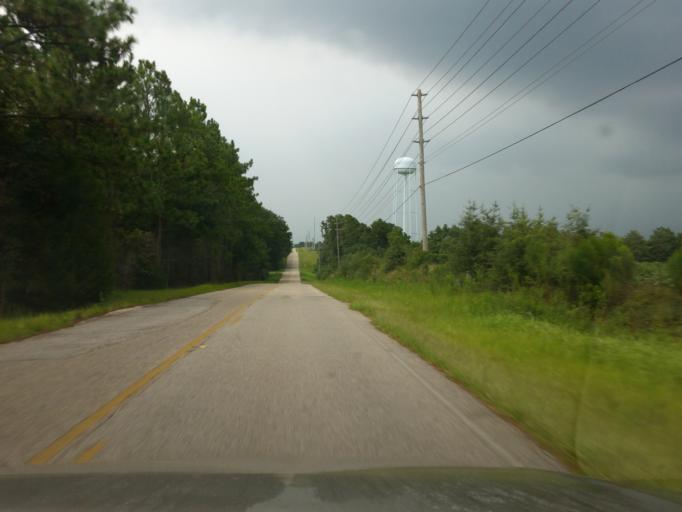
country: US
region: Alabama
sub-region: Baldwin County
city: Robertsdale
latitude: 30.5541
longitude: -87.5816
